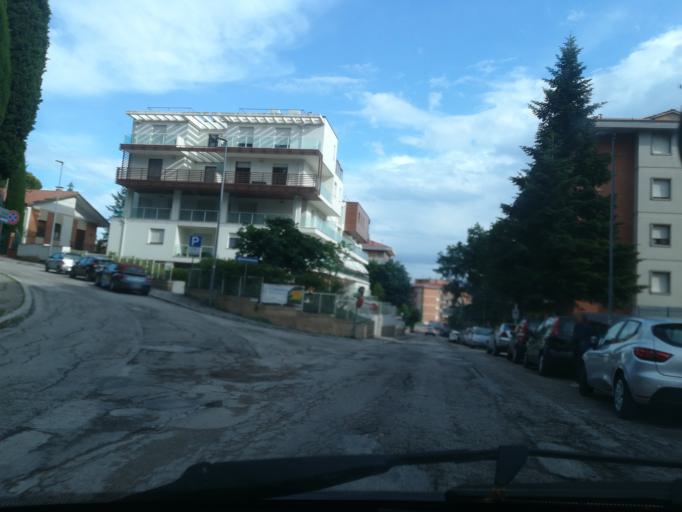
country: IT
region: The Marches
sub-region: Provincia di Macerata
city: Macerata
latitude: 43.2947
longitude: 13.4454
